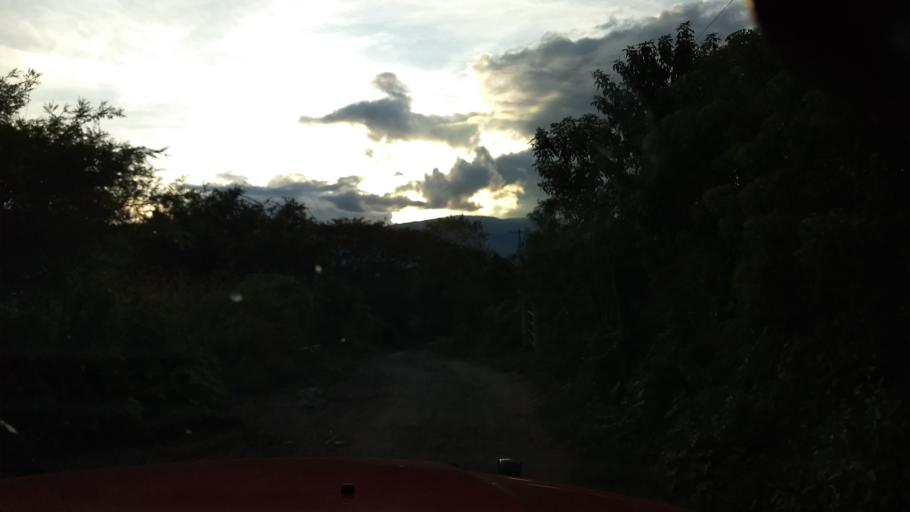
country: MX
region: Colima
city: Suchitlan
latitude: 19.4954
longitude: -103.7773
